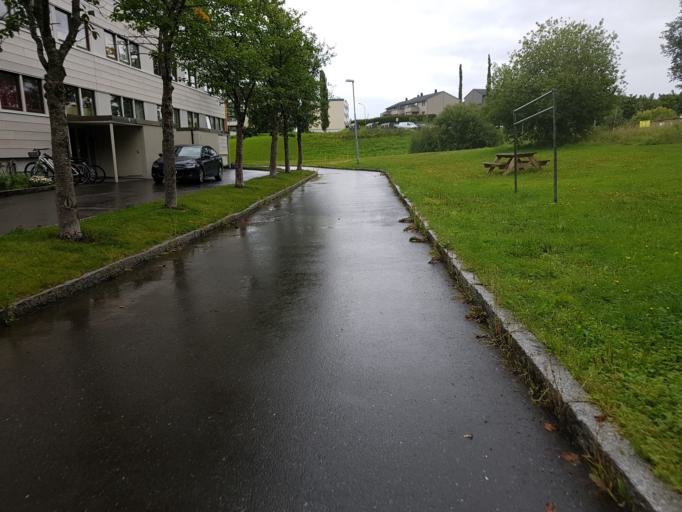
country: NO
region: Sor-Trondelag
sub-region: Trondheim
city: Trondheim
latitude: 63.4014
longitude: 10.4404
